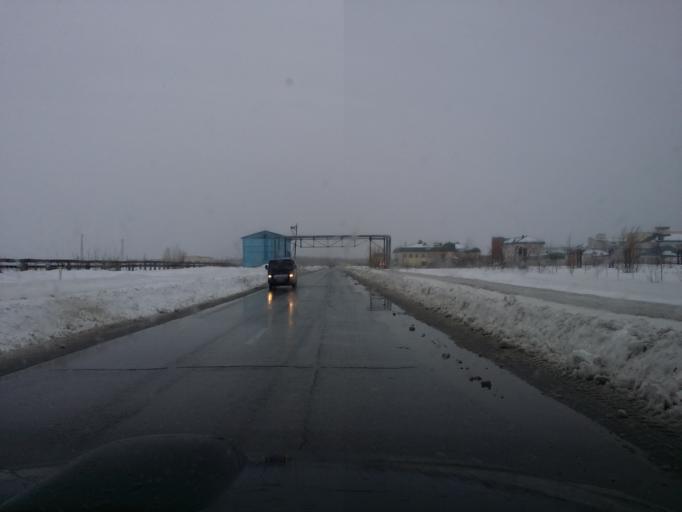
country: RU
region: Khanty-Mansiyskiy Avtonomnyy Okrug
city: Izluchinsk
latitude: 60.9802
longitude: 76.9160
